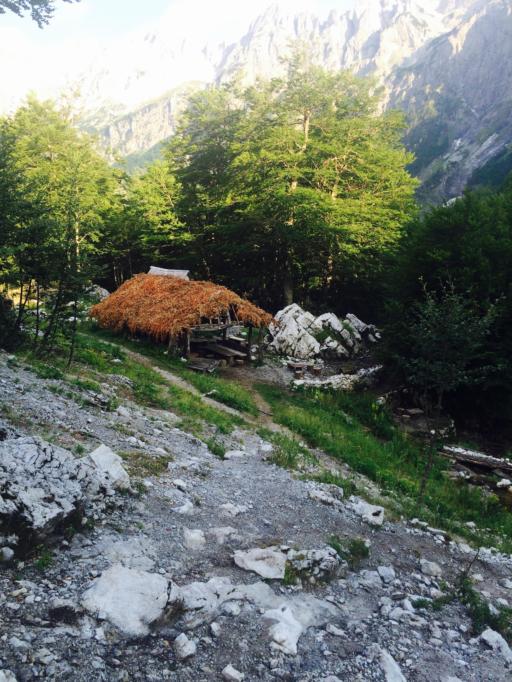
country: AL
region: Kukes
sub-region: Rrethi i Tropojes
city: Valbone
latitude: 42.4105
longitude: 19.8225
